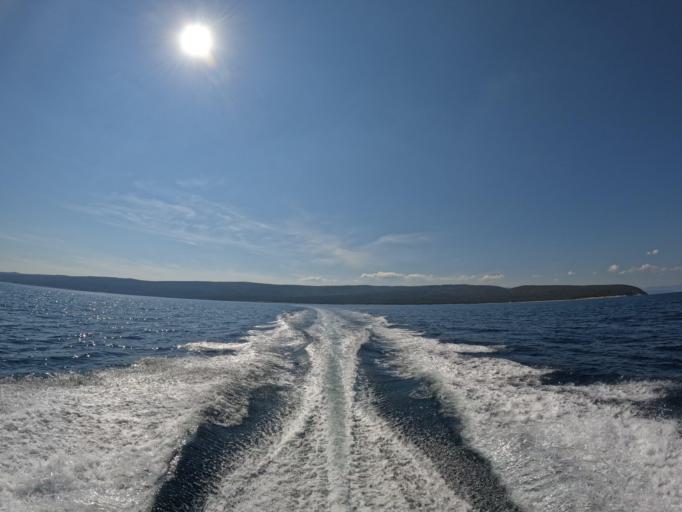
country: HR
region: Primorsko-Goranska
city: Cres
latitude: 44.9455
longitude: 14.4984
